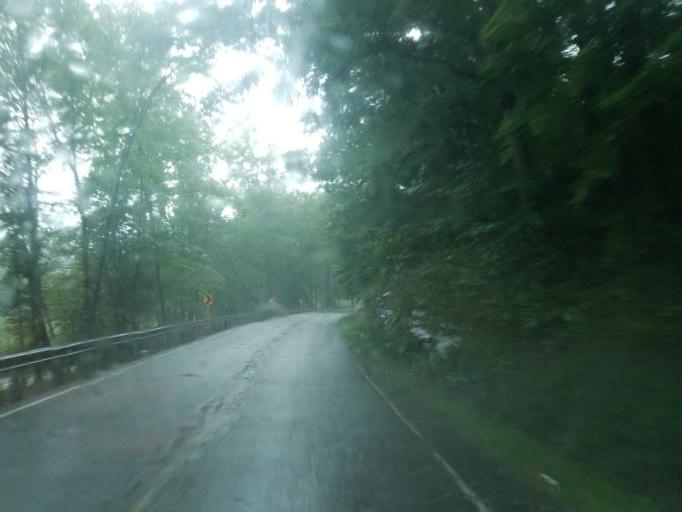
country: US
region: Kentucky
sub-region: Rowan County
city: Morehead
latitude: 38.2633
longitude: -83.3331
